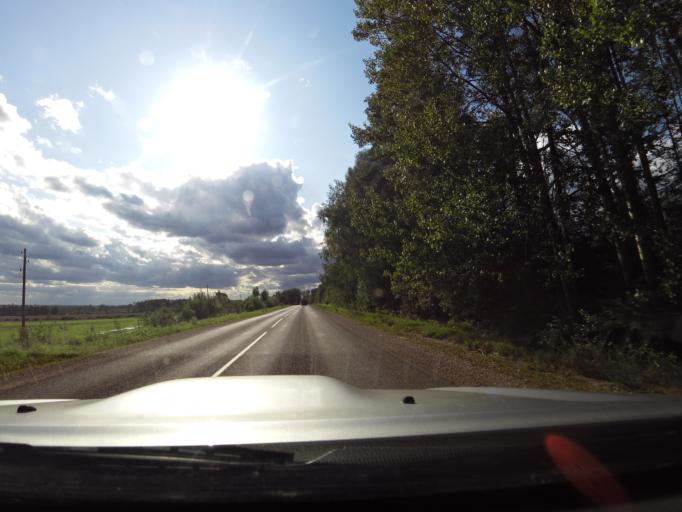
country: LV
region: Ilukste
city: Ilukste
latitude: 55.9669
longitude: 26.1828
